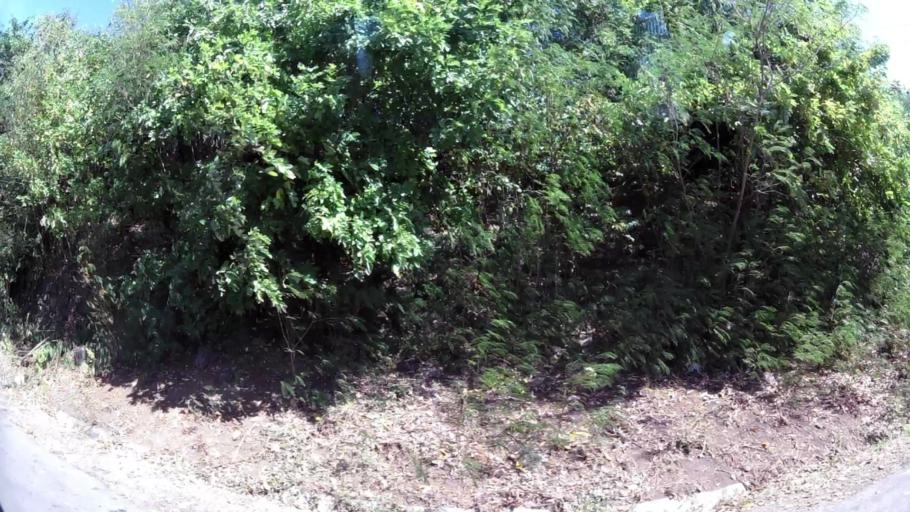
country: LC
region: Vieux-Fort
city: Vieux Fort
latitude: 13.7235
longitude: -60.9518
